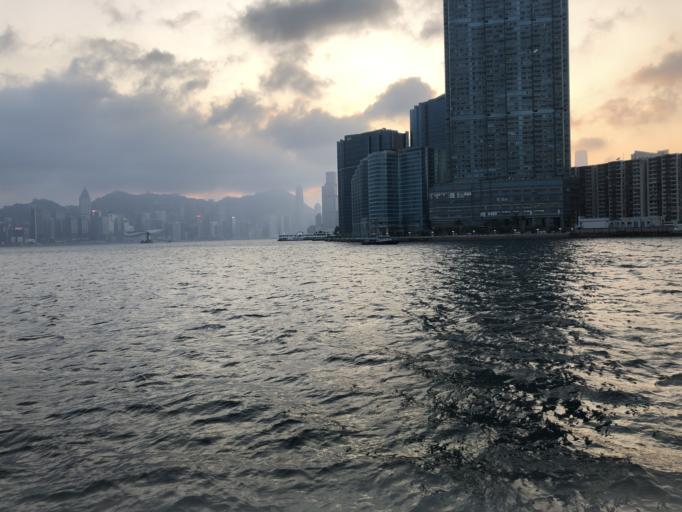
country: HK
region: Kowloon City
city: Kowloon
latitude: 22.3039
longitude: 114.1963
